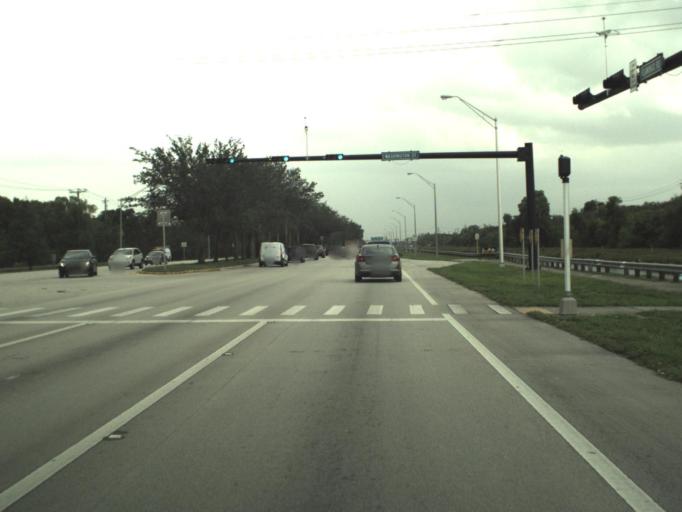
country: US
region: Florida
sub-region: Broward County
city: Sunshine Ranches
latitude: 26.0008
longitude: -80.3119
